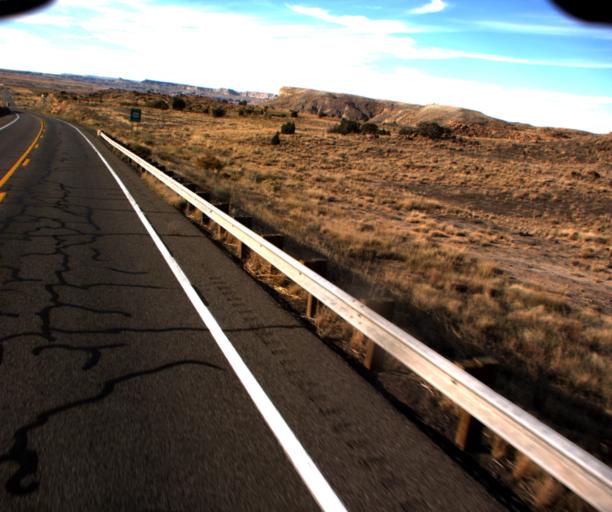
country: US
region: New Mexico
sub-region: San Juan County
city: Shiprock
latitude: 36.9152
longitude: -109.0774
